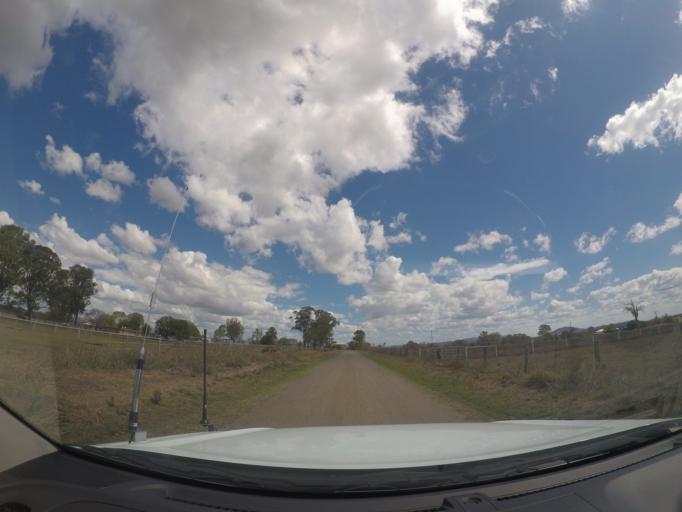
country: AU
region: Queensland
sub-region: Logan
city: Cedar Vale
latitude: -27.8955
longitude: 152.9586
